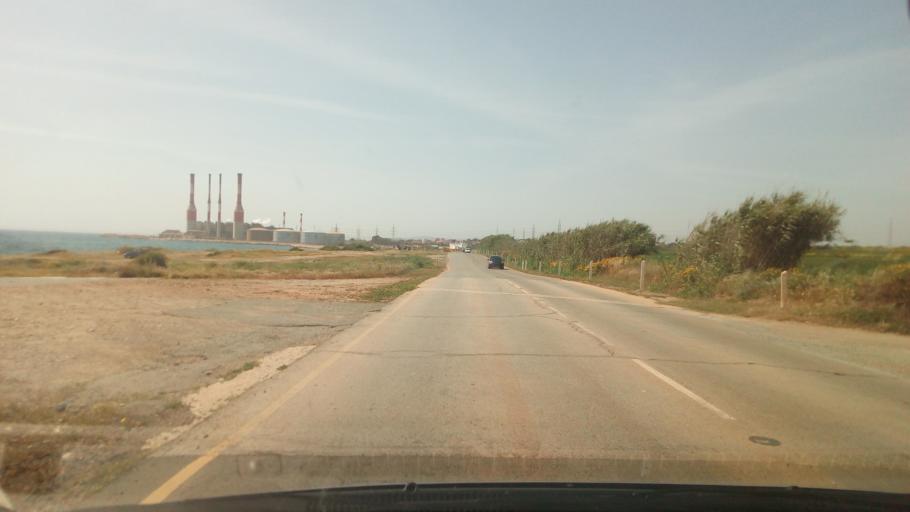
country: CY
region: Larnaka
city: Xylotymbou
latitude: 34.9820
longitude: 33.7589
